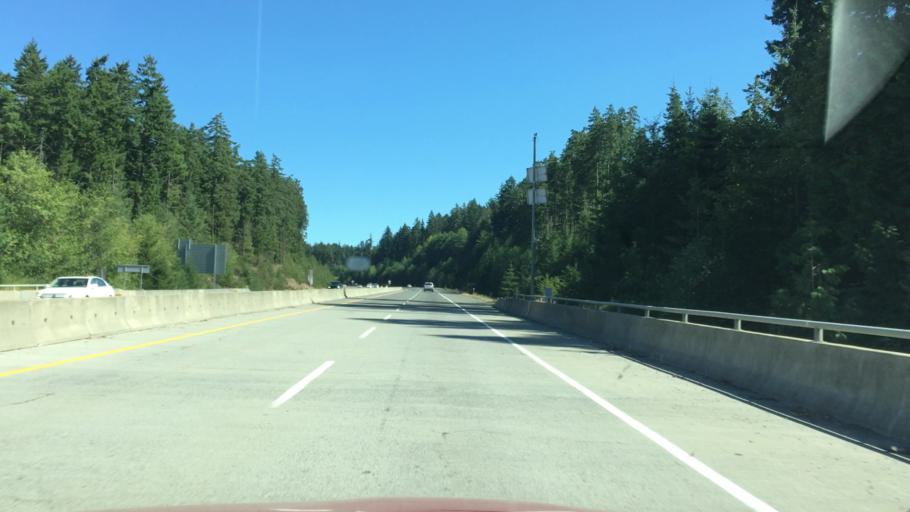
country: CA
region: British Columbia
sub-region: Regional District of Nanaimo
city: Parksville
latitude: 49.3225
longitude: -124.4117
